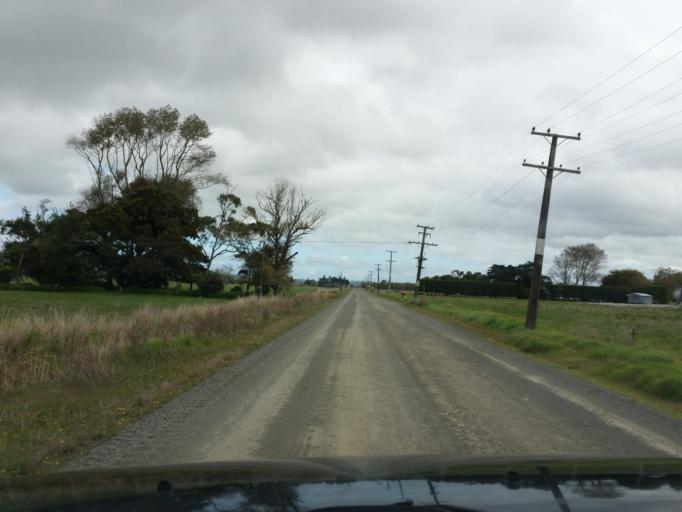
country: NZ
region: Northland
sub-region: Kaipara District
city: Dargaville
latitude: -36.0866
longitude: 174.0237
